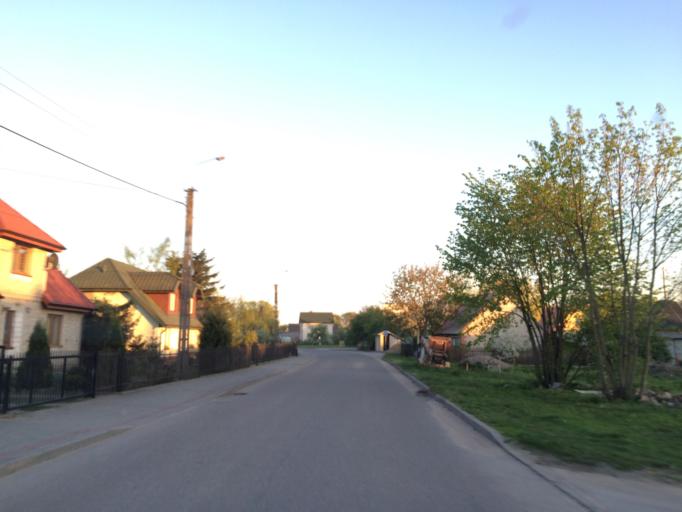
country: PL
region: Warmian-Masurian Voivodeship
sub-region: Powiat dzialdowski
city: Rybno
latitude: 53.4490
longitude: 19.9024
